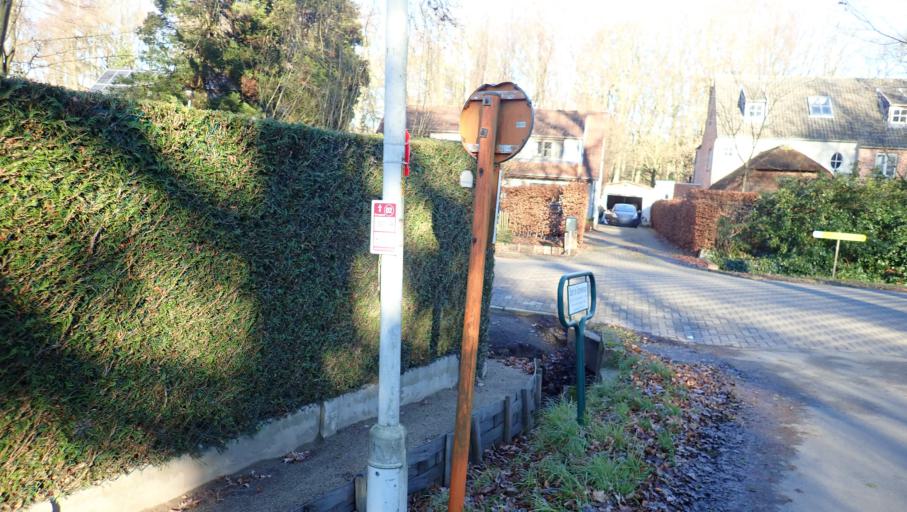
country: BE
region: Flanders
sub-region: Provincie Antwerpen
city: Schilde
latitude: 51.2510
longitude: 4.6250
